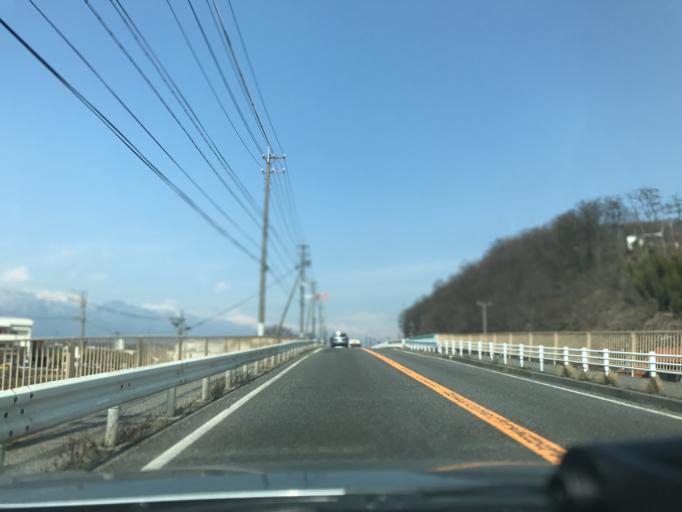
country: JP
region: Nagano
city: Matsumoto
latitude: 36.2416
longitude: 137.9544
